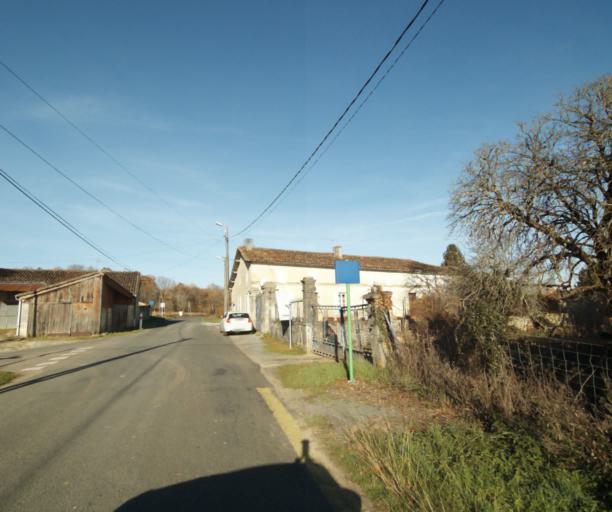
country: FR
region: Poitou-Charentes
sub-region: Departement de la Charente-Maritime
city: Cherac
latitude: 45.7099
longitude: -0.4497
